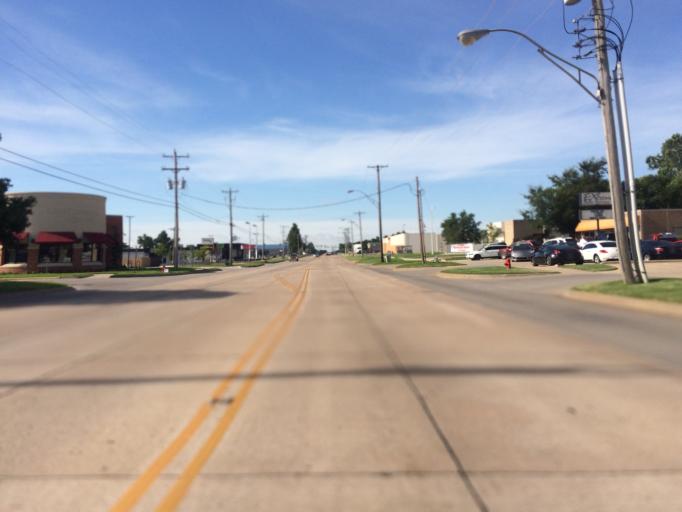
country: US
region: Oklahoma
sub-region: Cleveland County
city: Norman
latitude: 35.2227
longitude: -97.4767
